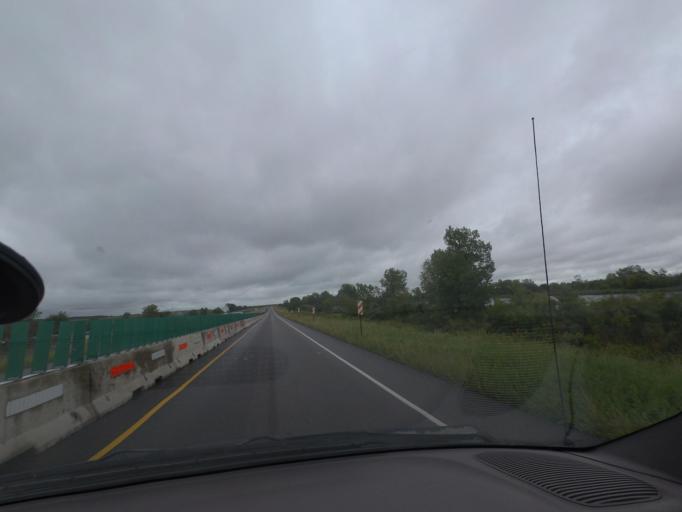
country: US
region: Illinois
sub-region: Piatt County
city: Cerro Gordo
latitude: 40.0010
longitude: -88.7787
